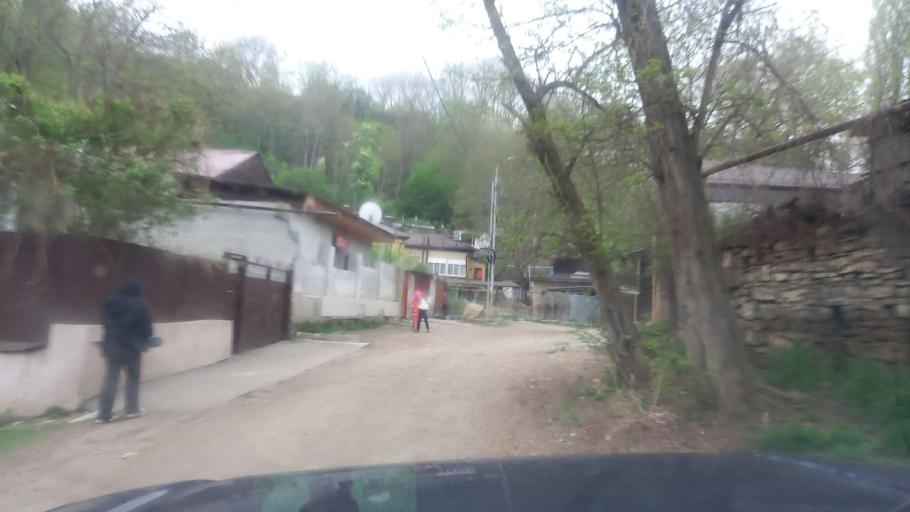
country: RU
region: Stavropol'skiy
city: Kislovodsk
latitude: 43.8910
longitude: 42.7097
